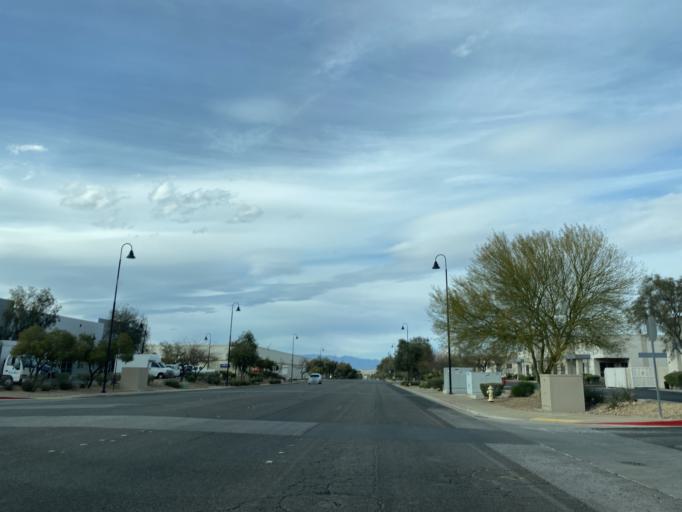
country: US
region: Nevada
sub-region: Clark County
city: Henderson
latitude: 36.0489
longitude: -115.0197
